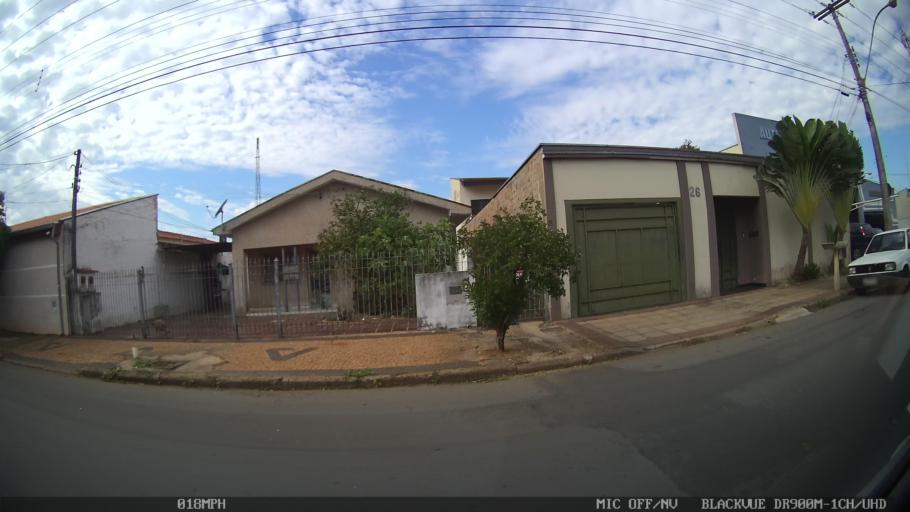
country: BR
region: Sao Paulo
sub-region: Americana
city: Americana
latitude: -22.7417
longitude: -47.3554
